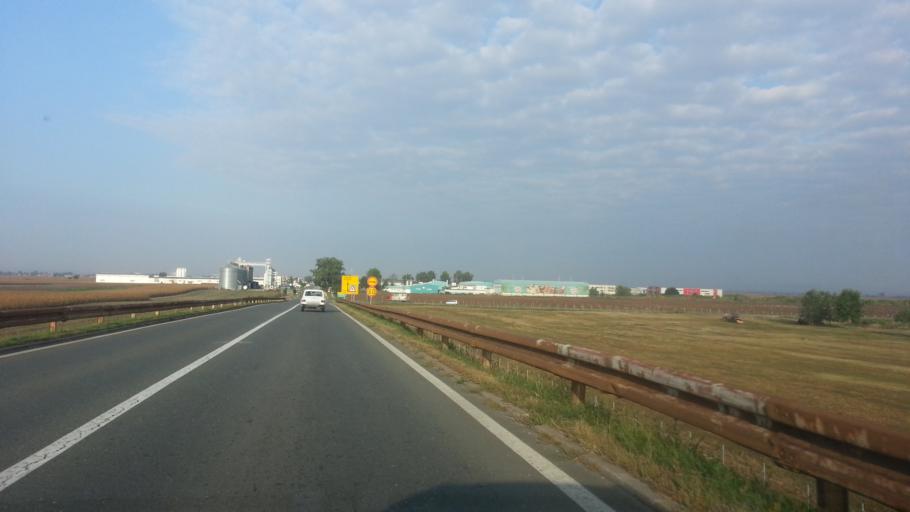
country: RS
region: Autonomna Pokrajina Vojvodina
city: Nova Pazova
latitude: 44.9867
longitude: 20.2136
